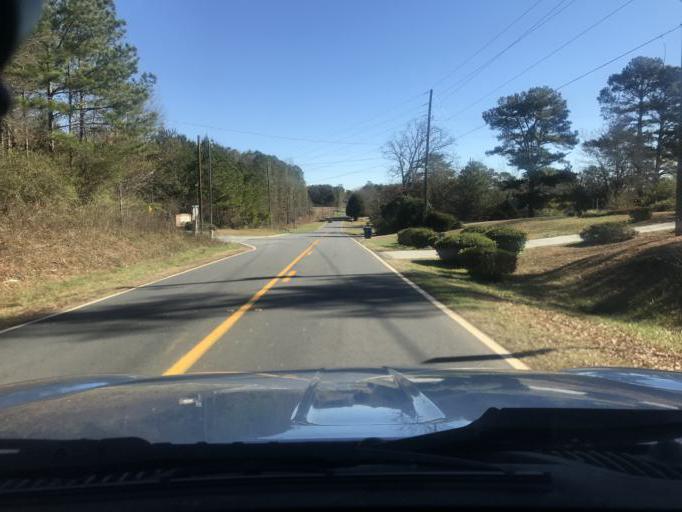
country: US
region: Georgia
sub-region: Barrow County
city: Russell
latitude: 33.9110
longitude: -83.7534
